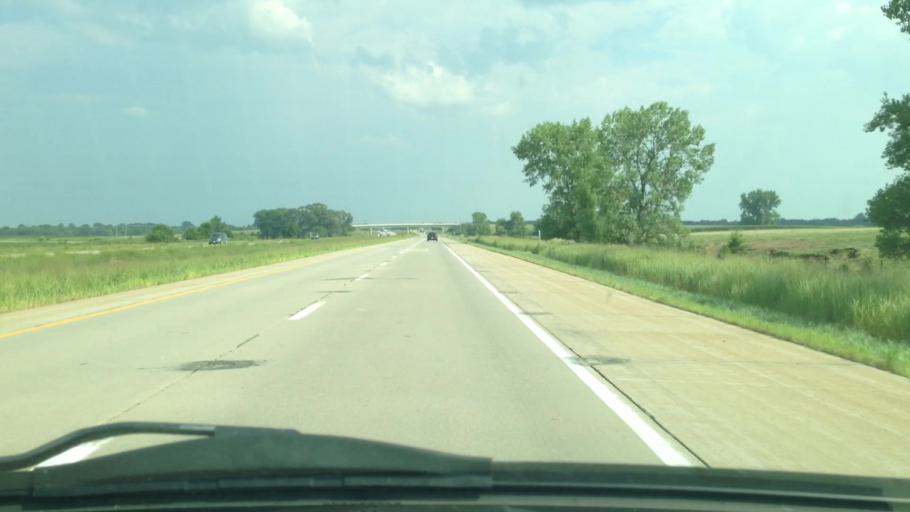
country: US
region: Iowa
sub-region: Black Hawk County
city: La Porte City
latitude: 42.3764
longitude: -92.1108
